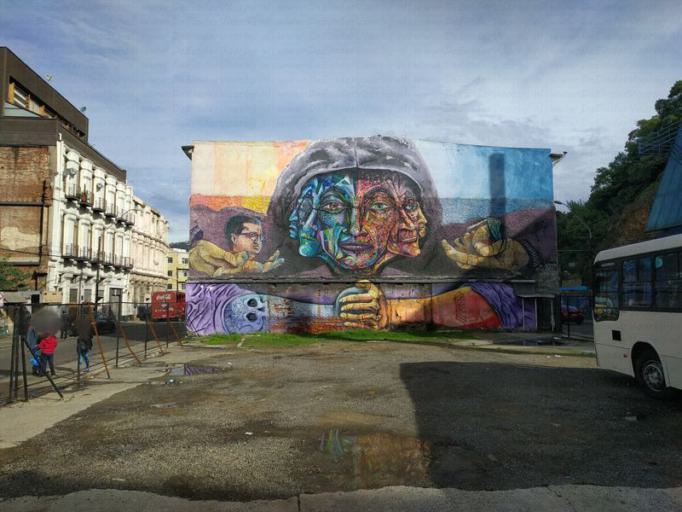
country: CL
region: Valparaiso
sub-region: Provincia de Valparaiso
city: Valparaiso
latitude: -33.0343
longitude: -71.6304
